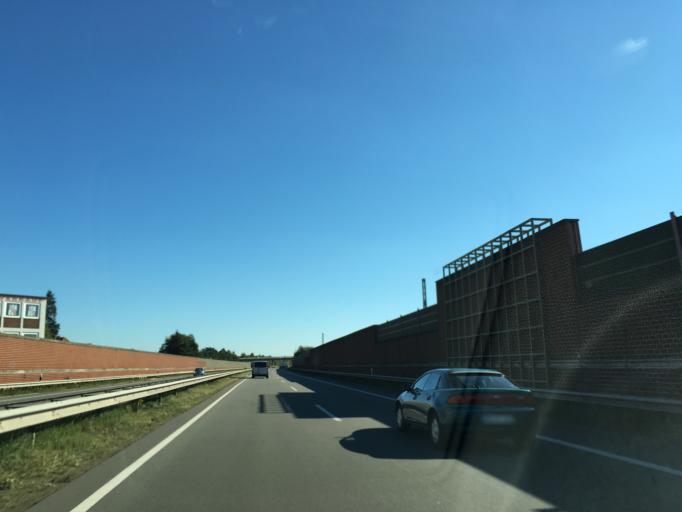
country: DE
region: Lower Saxony
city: Bardowick
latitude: 53.2909
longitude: 10.3716
